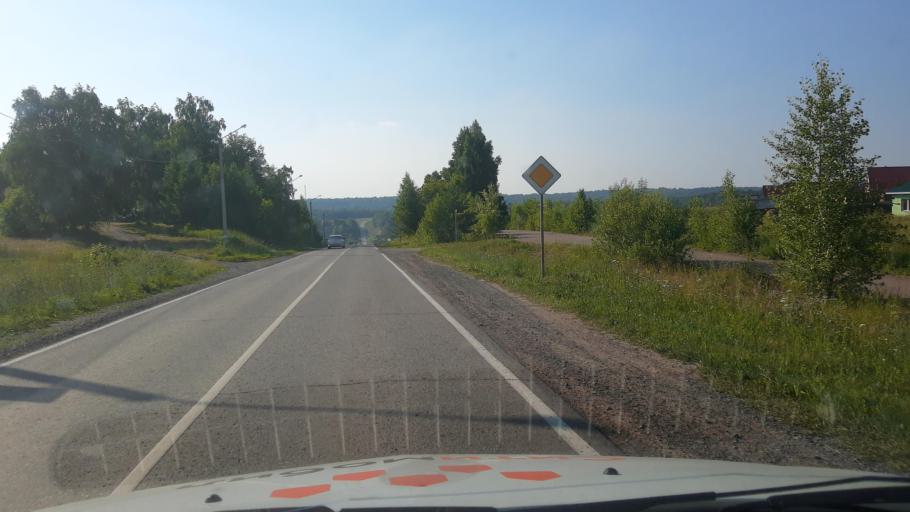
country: RU
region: Bashkortostan
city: Avdon
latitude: 54.6291
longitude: 55.6202
